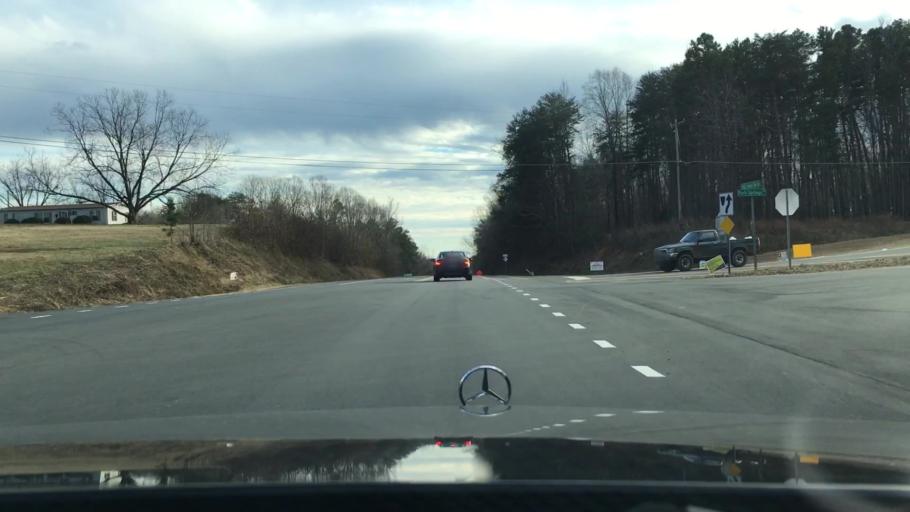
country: US
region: North Carolina
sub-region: Caswell County
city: Yanceyville
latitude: 36.4887
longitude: -79.3831
